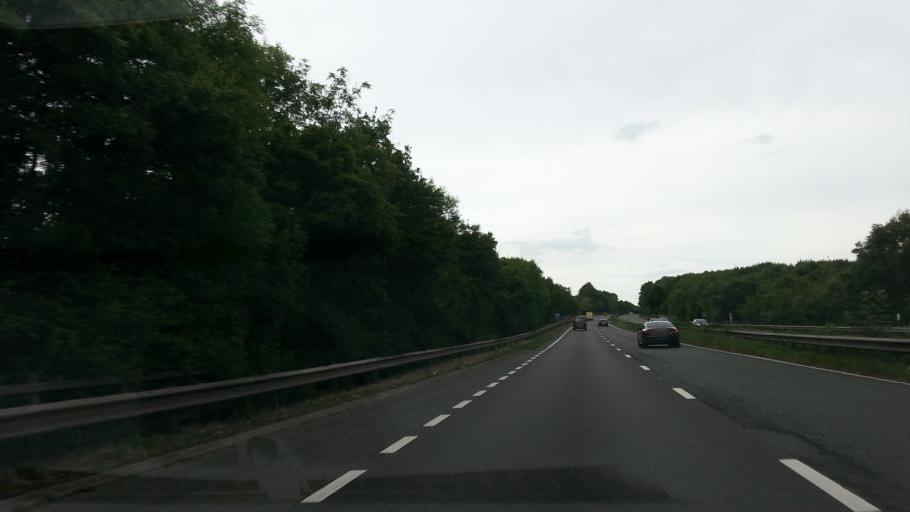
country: GB
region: England
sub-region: Herefordshire
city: Ross on Wye
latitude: 51.9205
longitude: -2.5914
